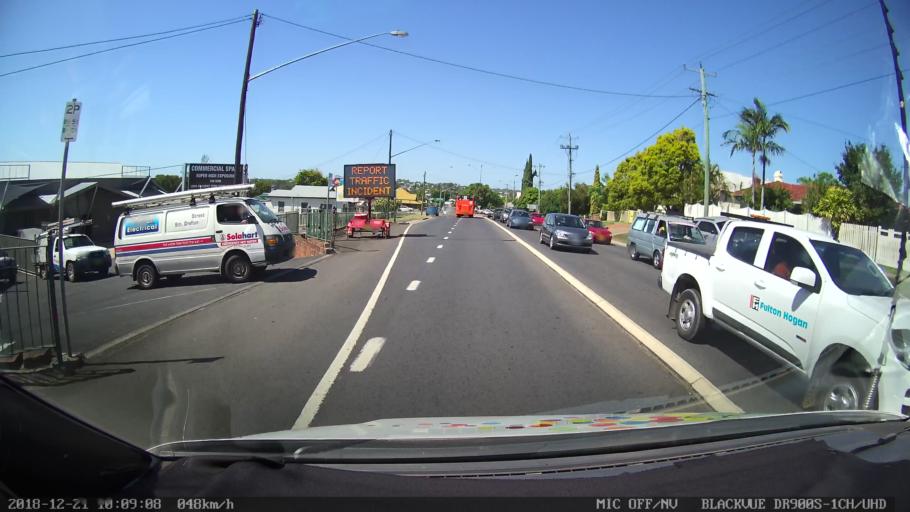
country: AU
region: New South Wales
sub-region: Clarence Valley
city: Grafton
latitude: -29.7027
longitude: 152.9411
